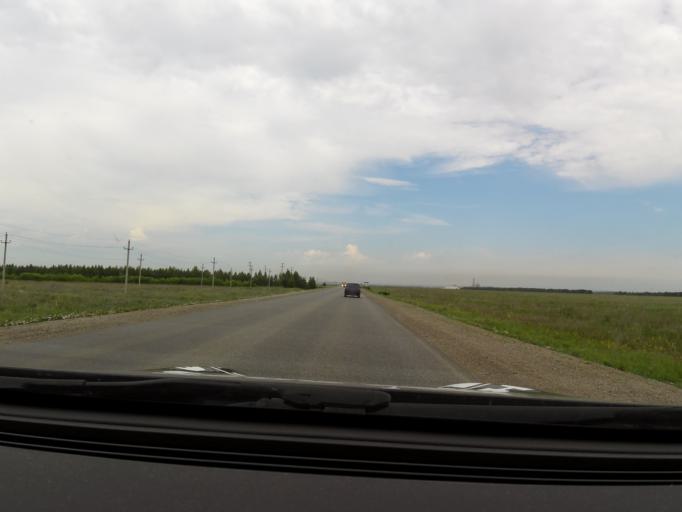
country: RU
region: Bashkortostan
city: Iglino
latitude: 54.7509
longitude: 56.2901
